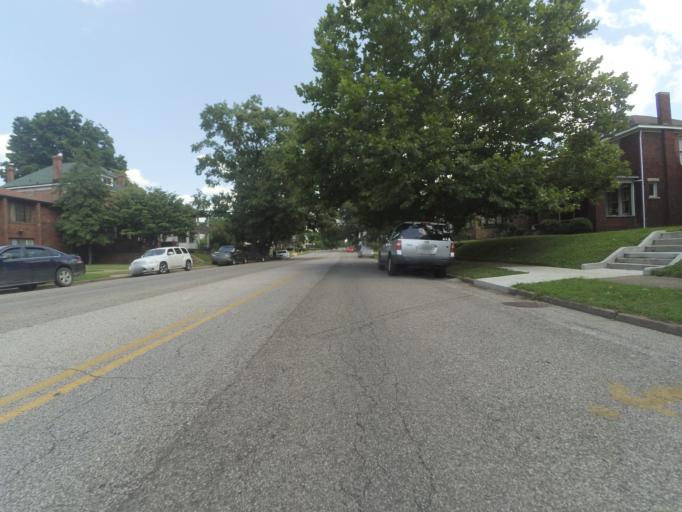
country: US
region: West Virginia
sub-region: Cabell County
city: Huntington
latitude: 38.4161
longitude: -82.4541
